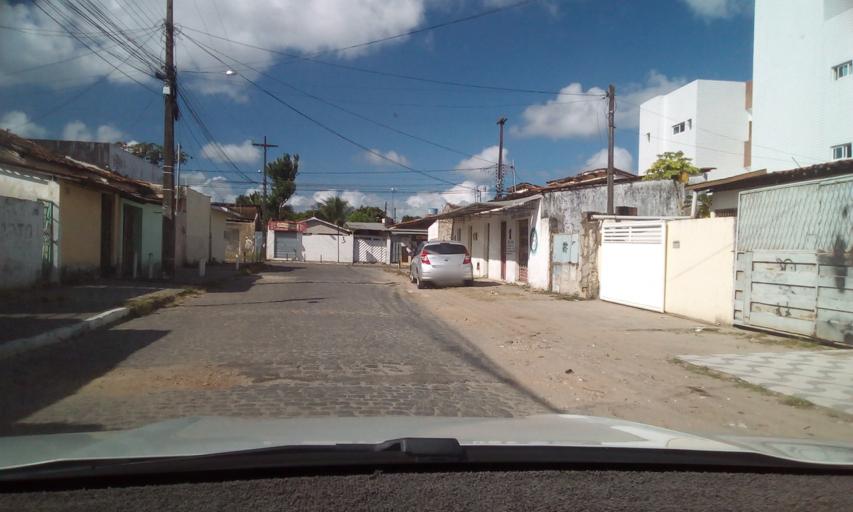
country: BR
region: Paraiba
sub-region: Joao Pessoa
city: Joao Pessoa
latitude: -7.1504
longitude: -34.8923
